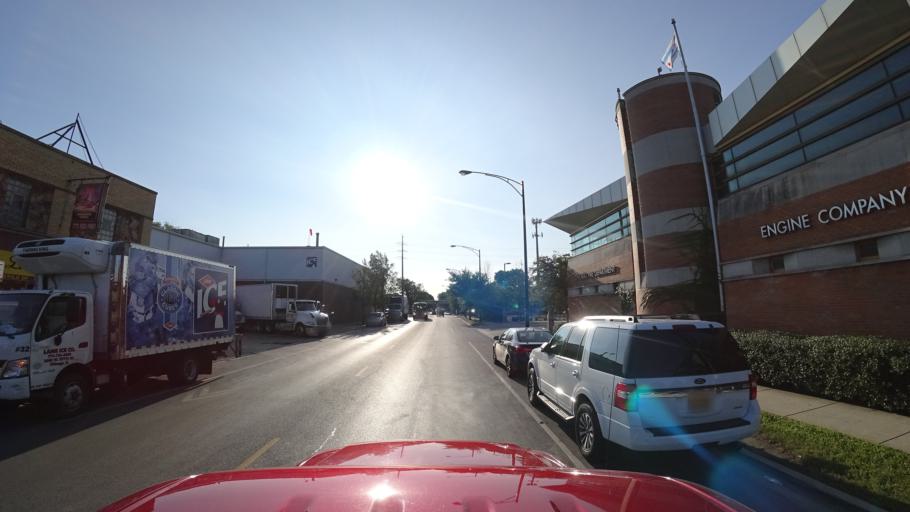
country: US
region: Illinois
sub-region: Cook County
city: Hometown
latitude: 41.7860
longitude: -87.7152
